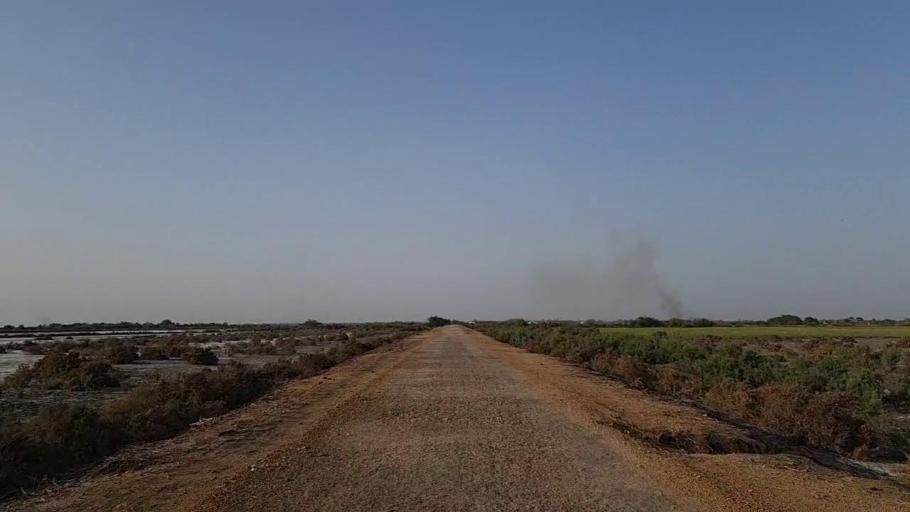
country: PK
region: Sindh
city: Jati
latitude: 24.3642
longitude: 68.1450
